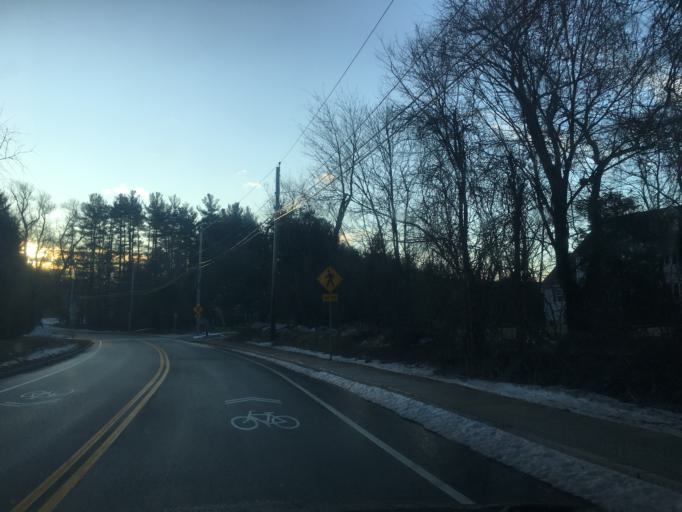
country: US
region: Massachusetts
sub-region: Middlesex County
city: Pinehurst
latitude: 42.5456
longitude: -71.2471
